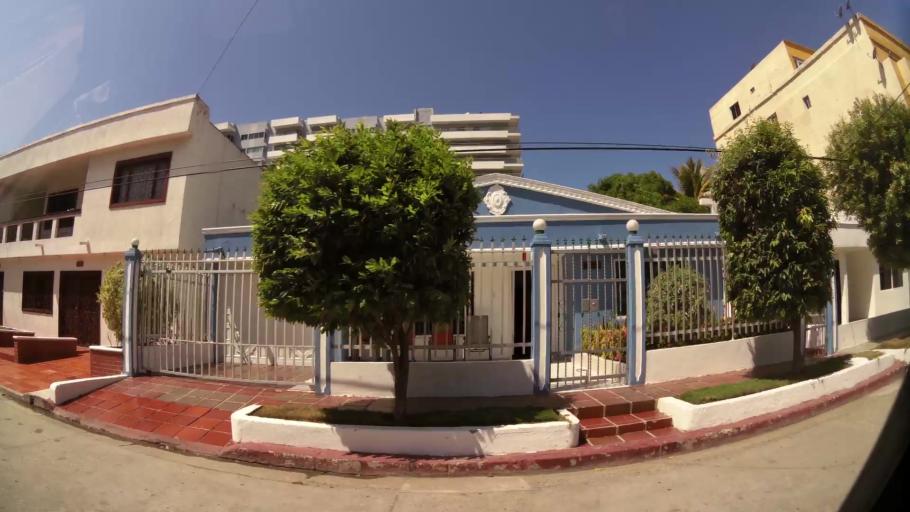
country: CO
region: Bolivar
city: Cartagena
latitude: 10.4509
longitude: -75.5151
